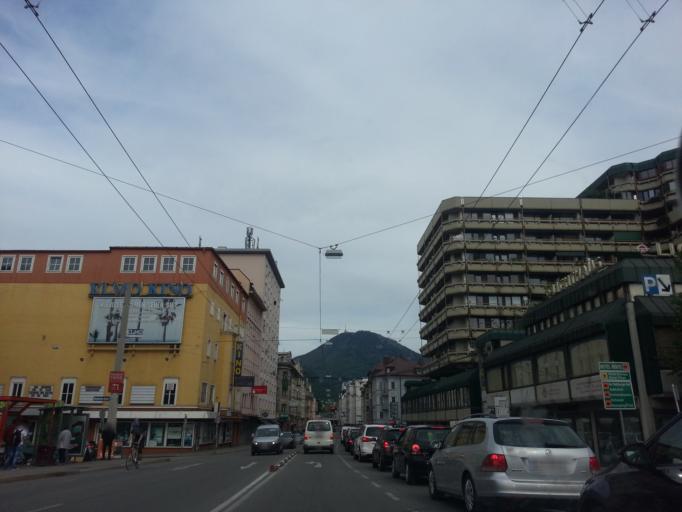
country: AT
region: Salzburg
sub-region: Salzburg Stadt
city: Salzburg
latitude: 47.8111
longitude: 13.0374
